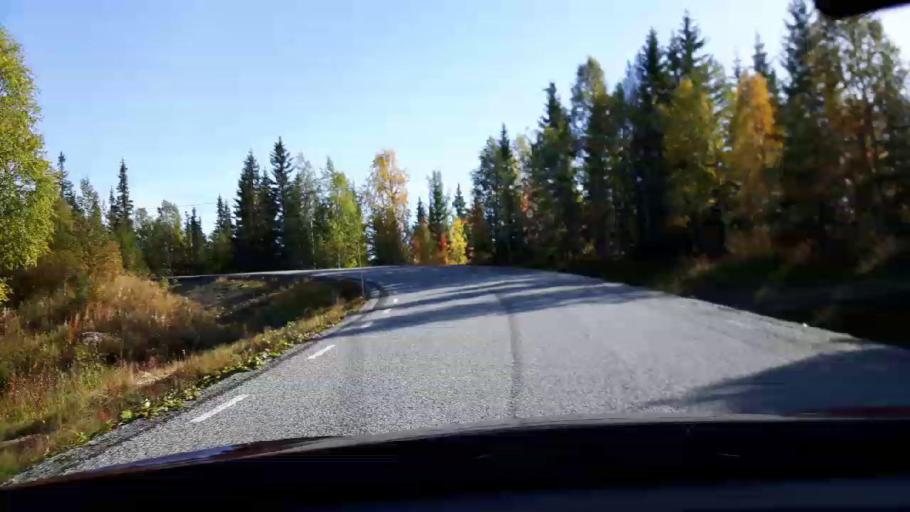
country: NO
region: Nord-Trondelag
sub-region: Royrvik
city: Royrvik
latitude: 64.8153
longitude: 14.1992
